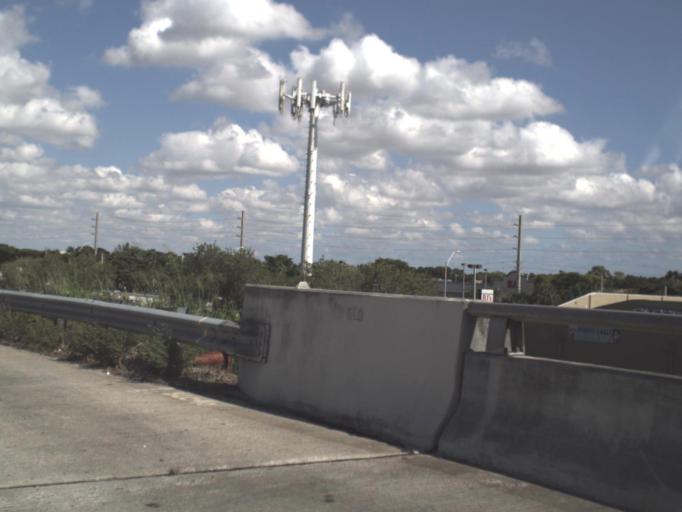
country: US
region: Florida
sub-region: Miami-Dade County
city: Kendale Lakes
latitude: 25.7011
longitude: -80.3835
